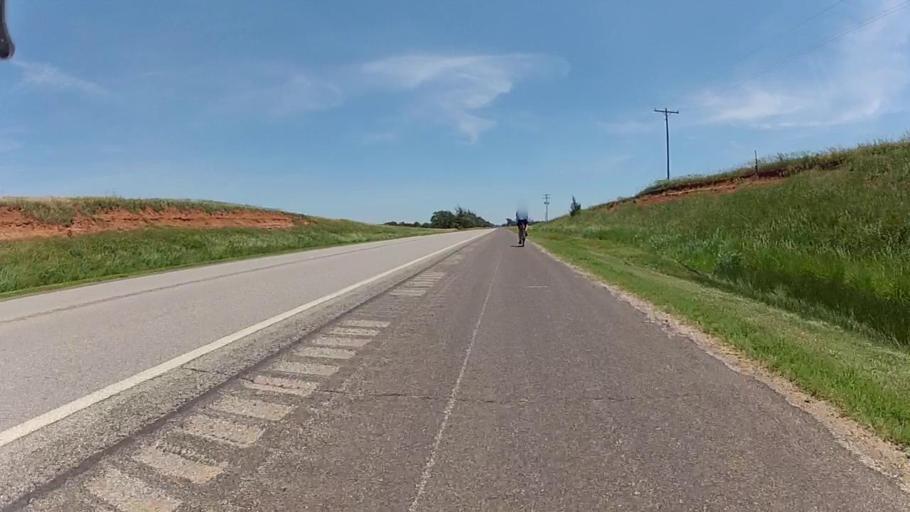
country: US
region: Kansas
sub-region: Barber County
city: Medicine Lodge
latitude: 37.2536
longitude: -98.3887
